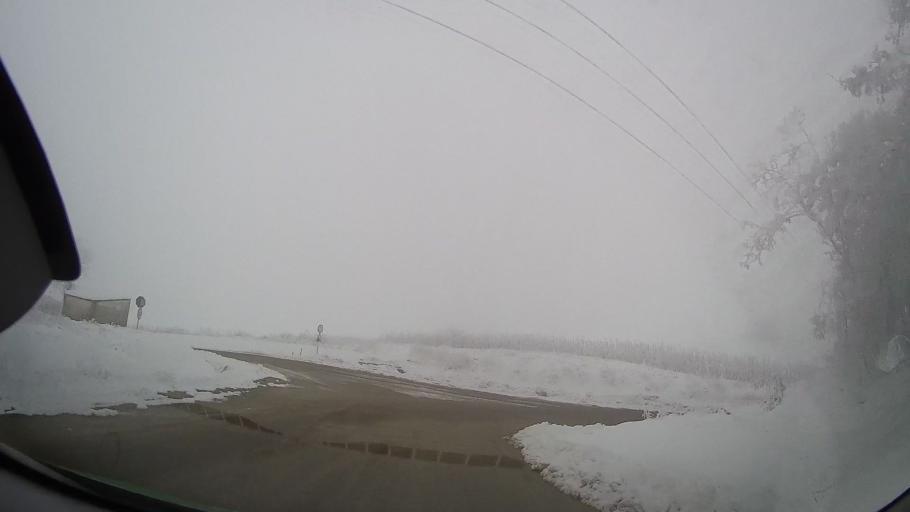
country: RO
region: Iasi
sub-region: Comuna Tansa
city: Suhulet
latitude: 46.8958
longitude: 27.2439
